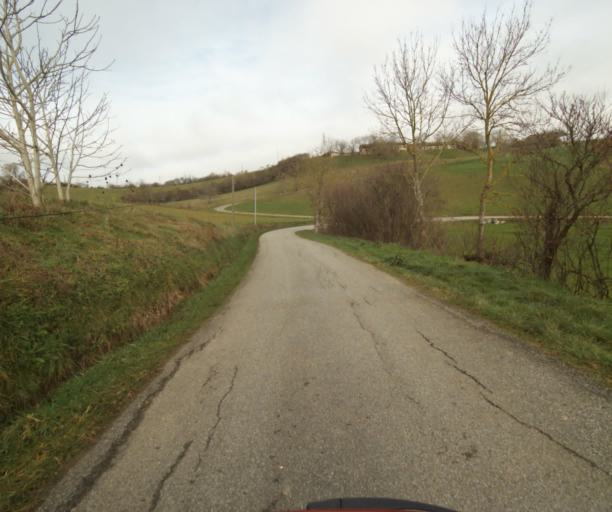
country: FR
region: Midi-Pyrenees
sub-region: Departement de l'Ariege
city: Saverdun
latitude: 43.1699
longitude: 1.5103
